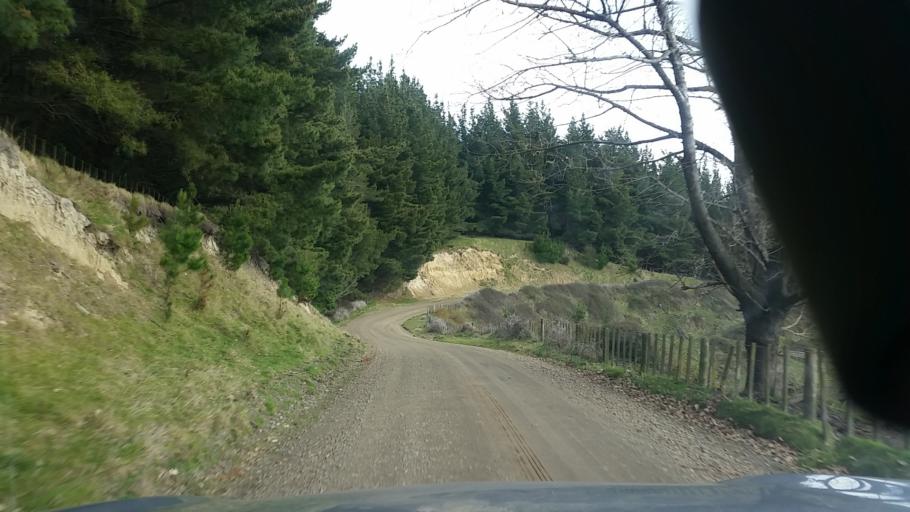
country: NZ
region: Hawke's Bay
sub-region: Napier City
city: Napier
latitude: -39.2285
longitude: 176.9855
